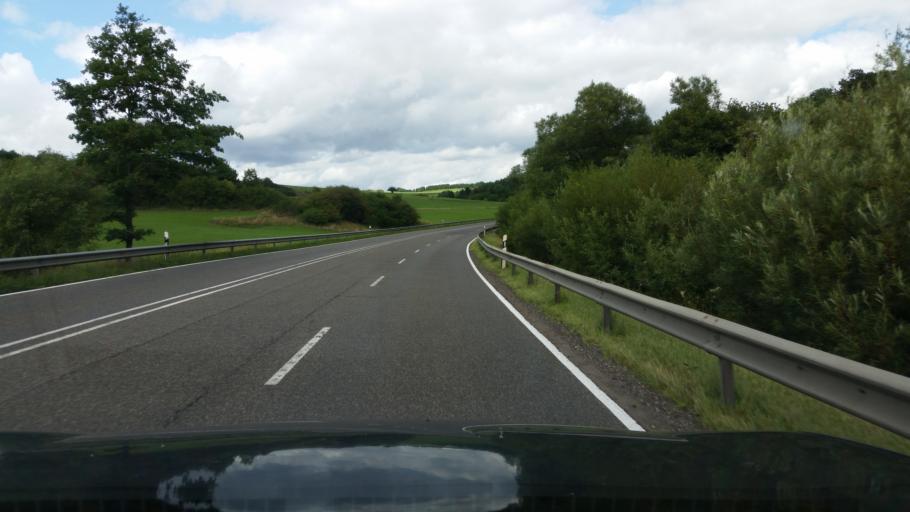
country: DE
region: Rheinland-Pfalz
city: Uxheim
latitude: 50.4002
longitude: 6.7356
